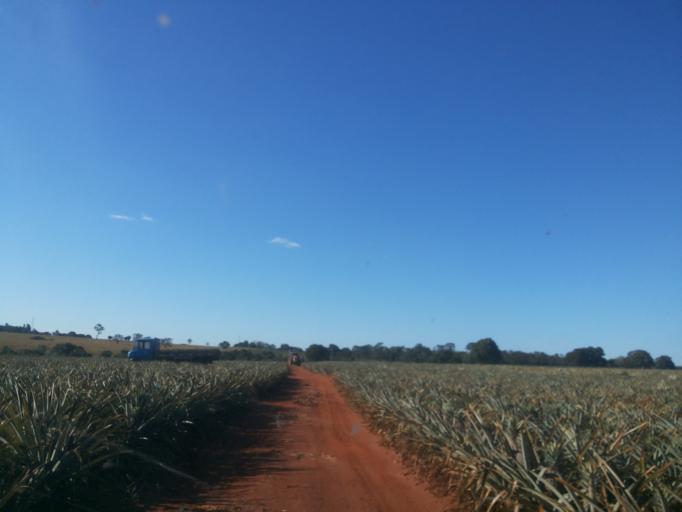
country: BR
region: Minas Gerais
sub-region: Centralina
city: Centralina
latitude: -18.7524
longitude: -49.1016
